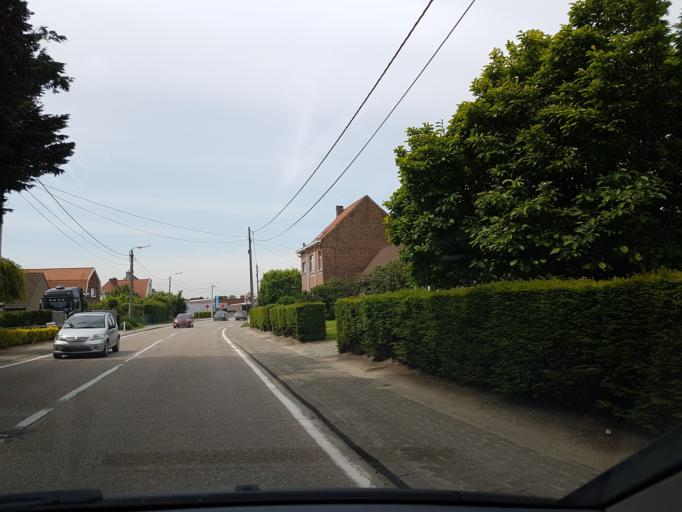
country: BE
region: Flanders
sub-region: Provincie Vlaams-Brabant
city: Asse
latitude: 50.9049
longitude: 4.1890
